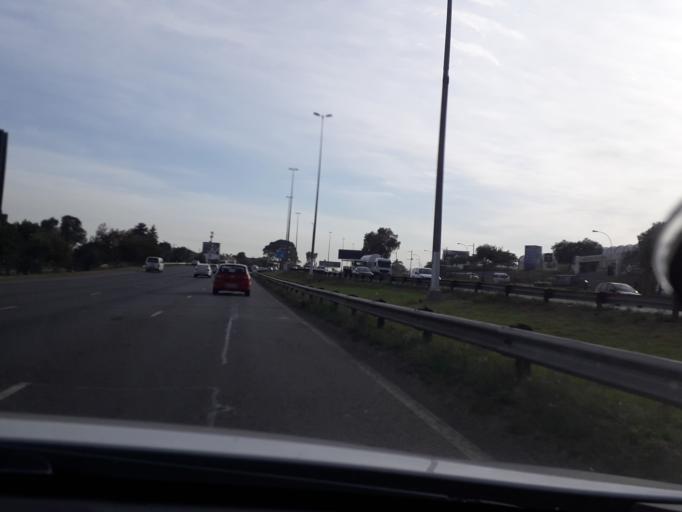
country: ZA
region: Gauteng
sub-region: City of Johannesburg Metropolitan Municipality
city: Modderfontein
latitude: -26.1528
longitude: 28.1685
